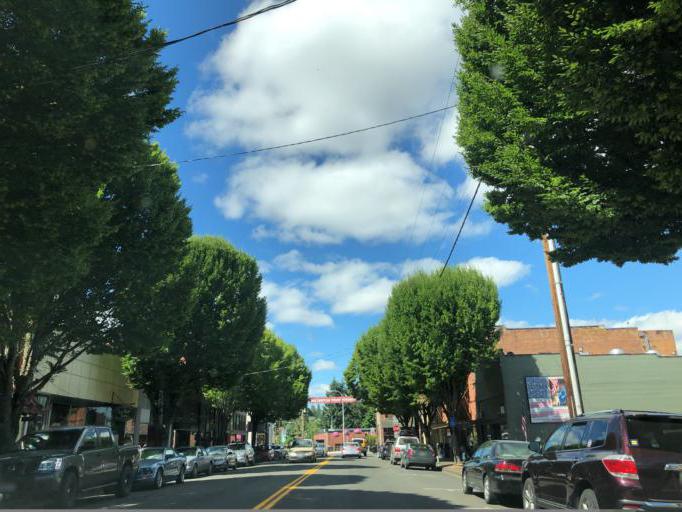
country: US
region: Oregon
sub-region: Marion County
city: Silverton
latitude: 45.0055
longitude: -122.7822
